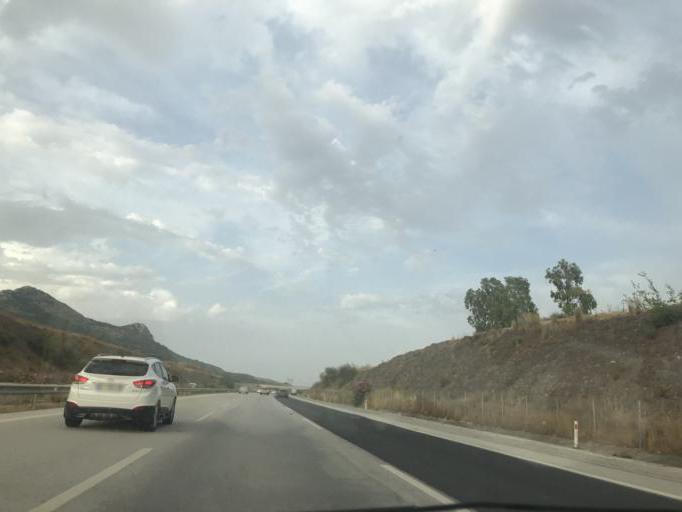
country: TR
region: Adana
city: Kosreli
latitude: 37.0128
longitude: 35.9698
